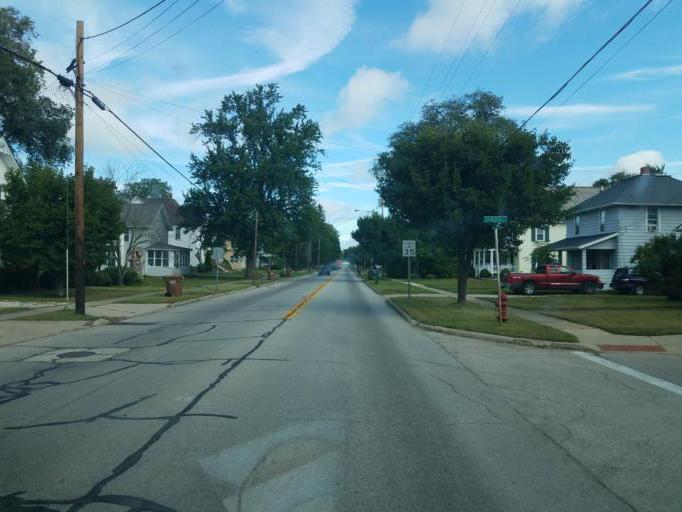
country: US
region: Ohio
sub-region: Lorain County
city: Wellington
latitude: 41.0956
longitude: -82.1234
